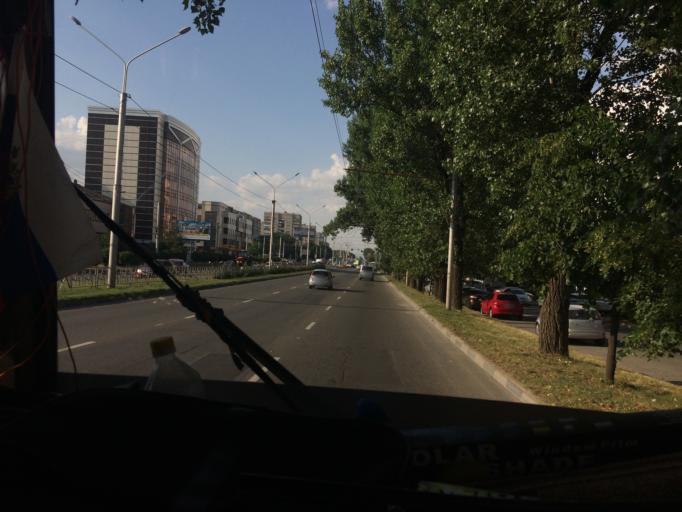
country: RU
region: Stavropol'skiy
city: Stavropol'
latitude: 45.0168
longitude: 41.9320
